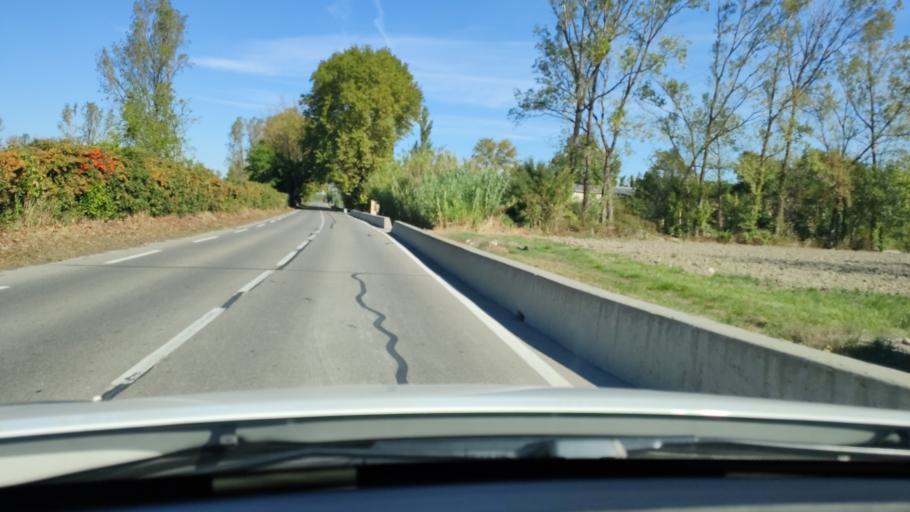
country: FR
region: Provence-Alpes-Cote d'Azur
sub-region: Departement du Vaucluse
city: Morieres-les-Avignon
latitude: 43.9156
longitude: 4.9070
